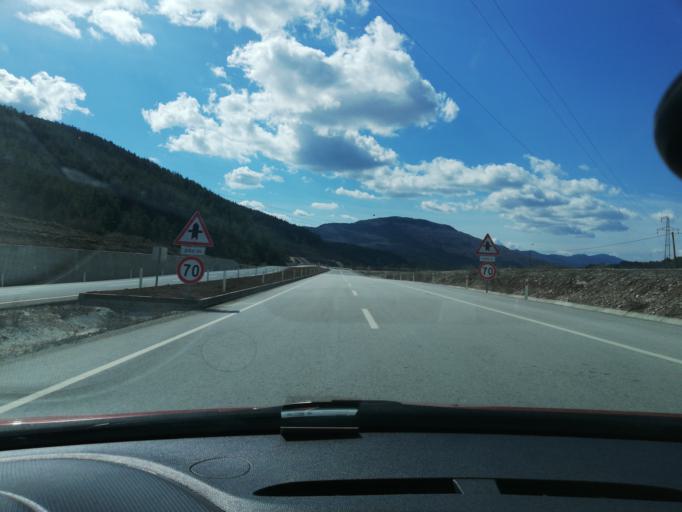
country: TR
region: Karabuk
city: Ovacik
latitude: 41.2092
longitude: 32.9585
